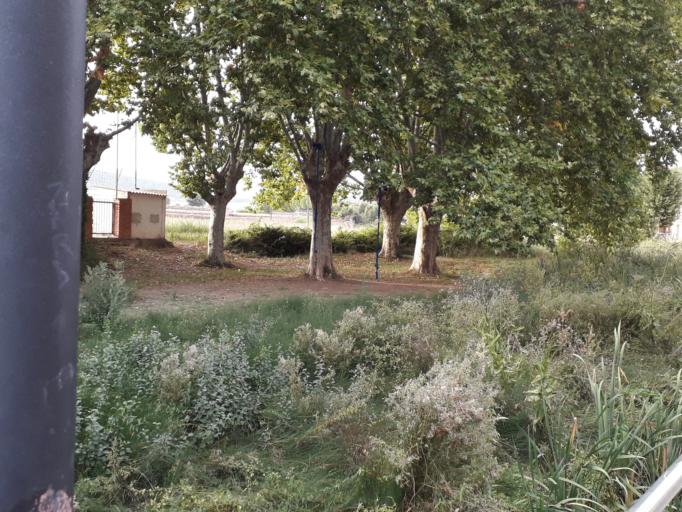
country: ES
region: Catalonia
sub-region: Provincia de Barcelona
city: Sant Joan de Mediona
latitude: 41.4780
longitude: 1.6100
